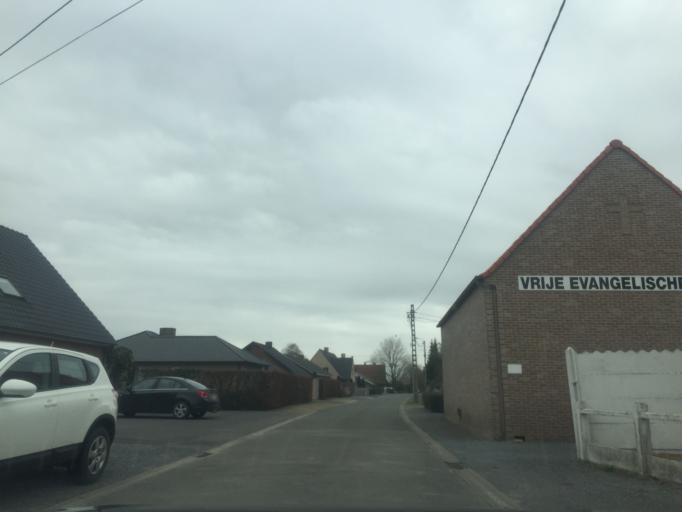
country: BE
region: Flanders
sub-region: Provincie West-Vlaanderen
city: Oostrozebeke
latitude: 50.9166
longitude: 3.3104
